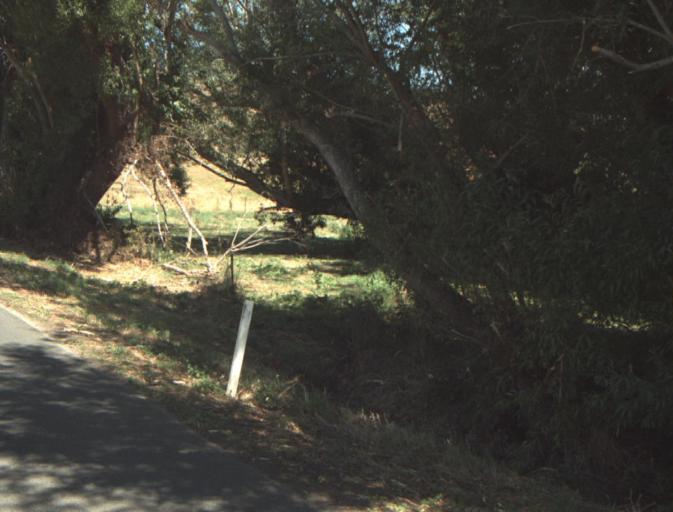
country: AU
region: Tasmania
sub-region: Launceston
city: Mayfield
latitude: -41.2640
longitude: 147.1349
